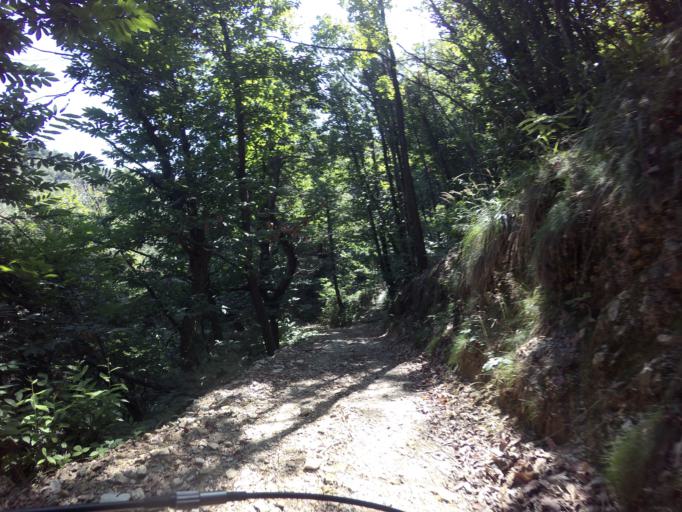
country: IT
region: Piedmont
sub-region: Provincia di Cuneo
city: Roccaforte Mondovi
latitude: 44.3255
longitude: 7.7118
